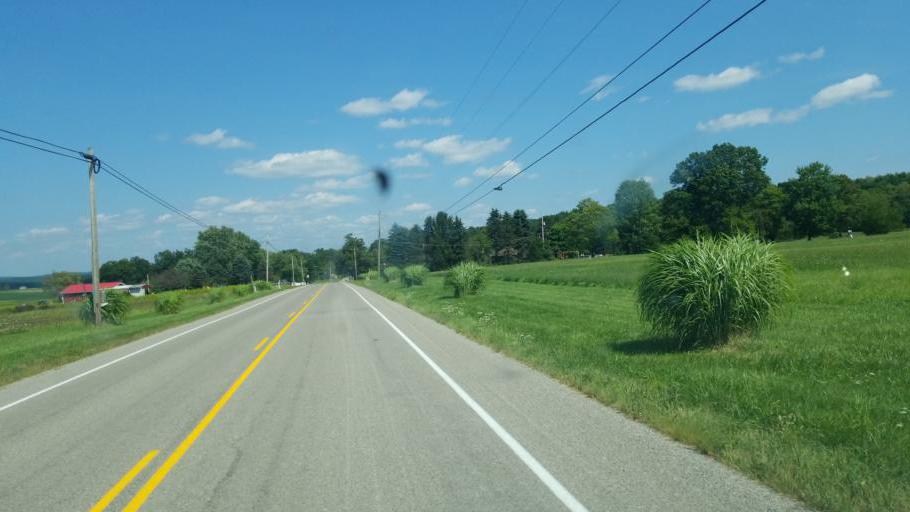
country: US
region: Pennsylvania
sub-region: Clarion County
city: Knox
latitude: 41.1175
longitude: -79.5833
